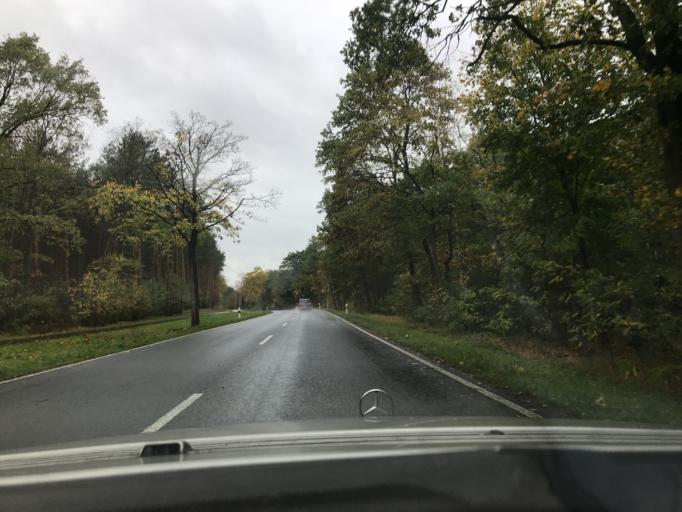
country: DE
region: Brandenburg
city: Trebbin
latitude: 52.2231
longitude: 13.1918
